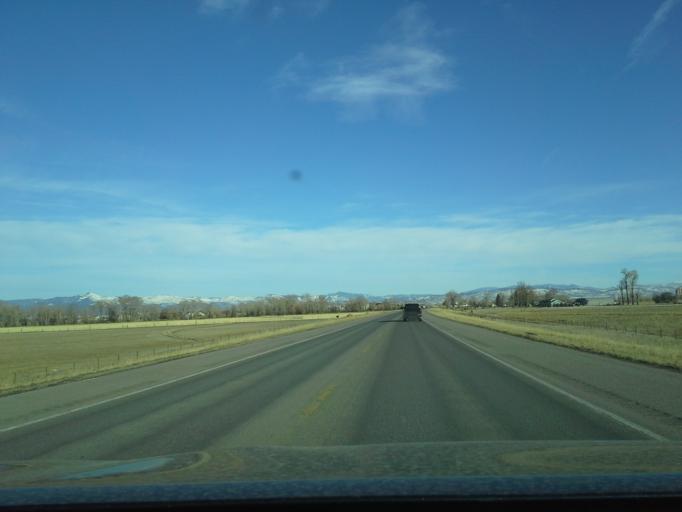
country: US
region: Montana
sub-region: Lewis and Clark County
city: Helena Valley Southeast
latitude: 46.6168
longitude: -111.9711
